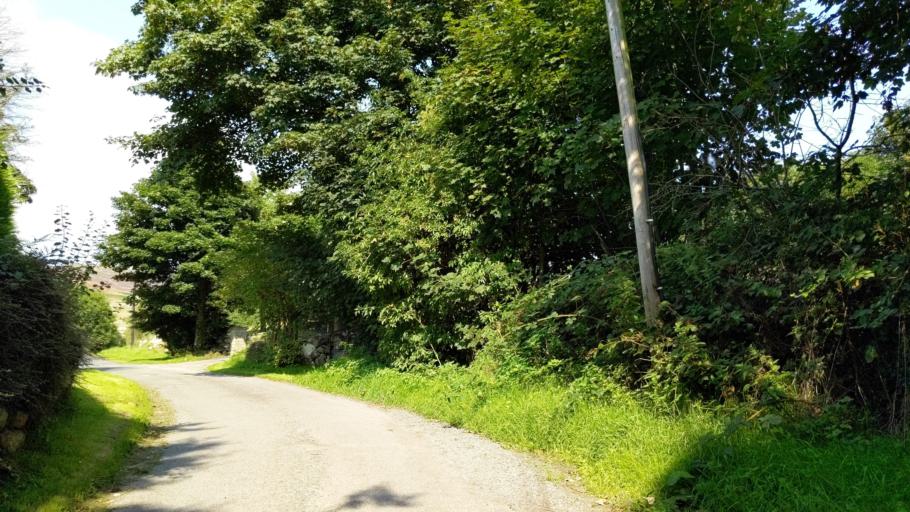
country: GB
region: Northern Ireland
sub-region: Down District
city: Warrenpoint
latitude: 54.0588
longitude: -6.3300
